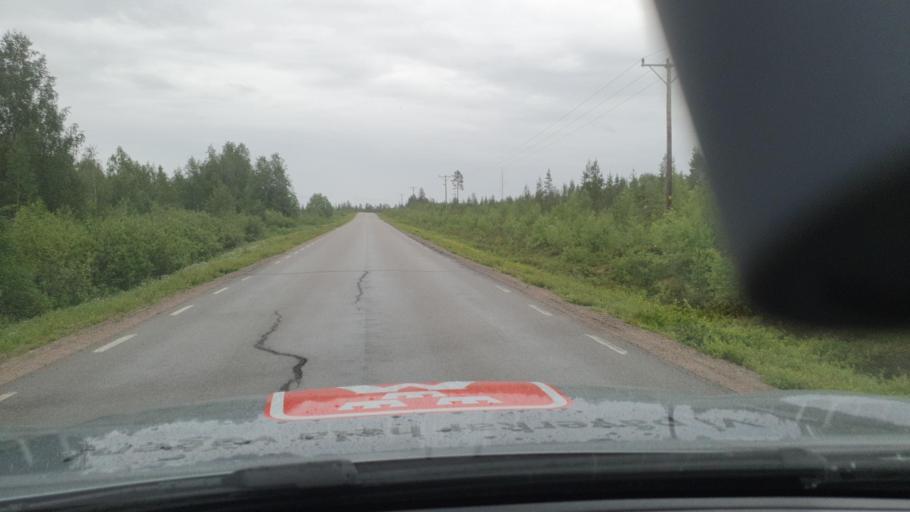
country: SE
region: Norrbotten
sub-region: Pajala Kommun
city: Pajala
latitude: 66.7872
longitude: 23.1286
